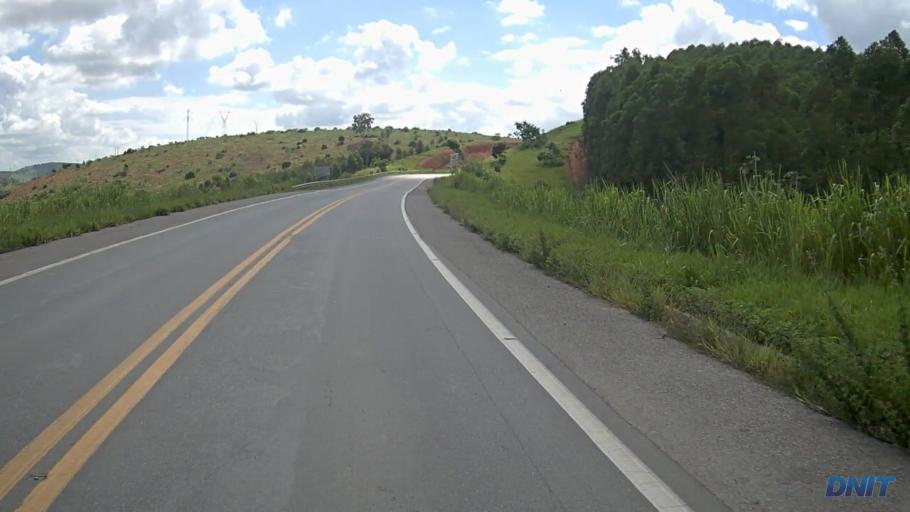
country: BR
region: Minas Gerais
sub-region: Governador Valadares
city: Governador Valadares
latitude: -19.0671
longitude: -42.1724
